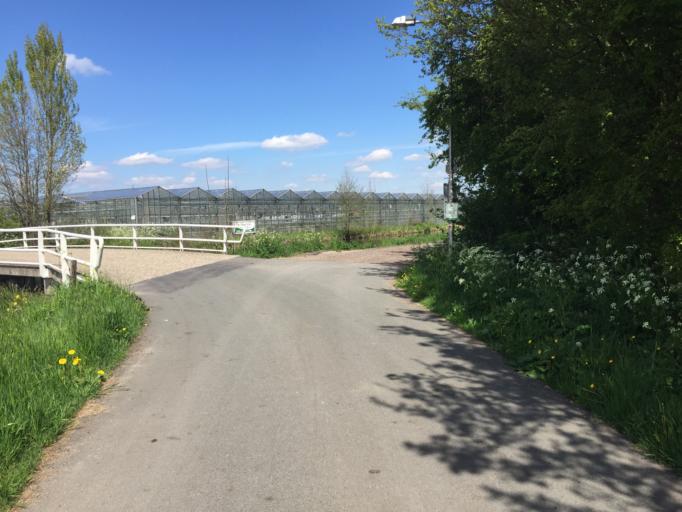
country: NL
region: South Holland
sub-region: Gemeente Nieuwkoop
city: Nieuwkoop
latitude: 52.1838
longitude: 4.7383
